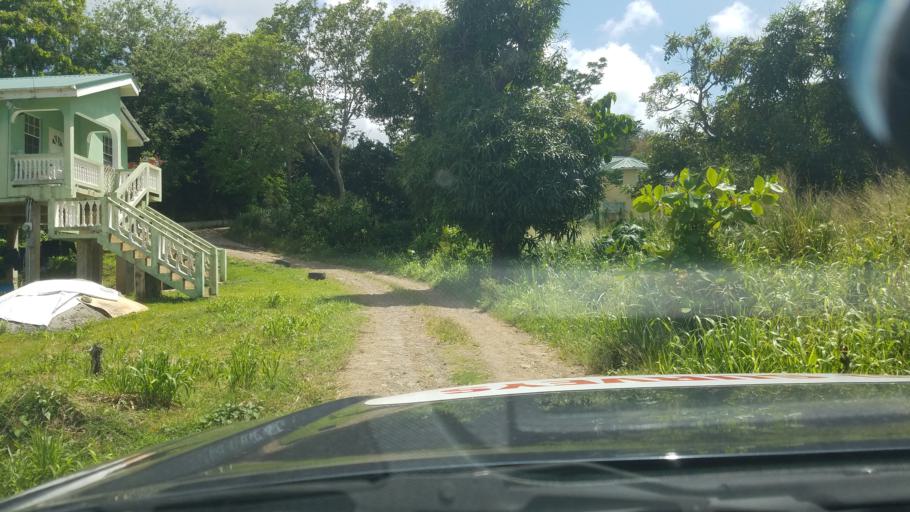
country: LC
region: Castries Quarter
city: Bisee
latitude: 14.0312
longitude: -60.9498
